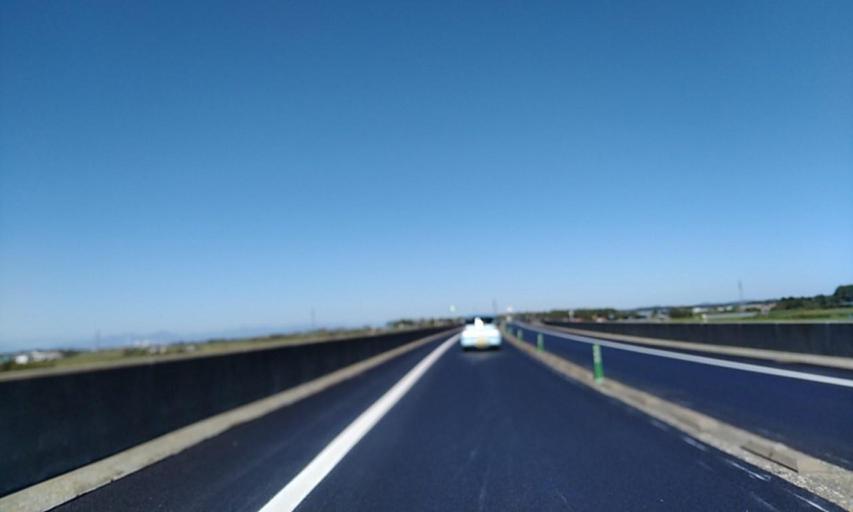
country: JP
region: Hokkaido
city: Tomakomai
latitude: 42.5827
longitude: 141.9460
